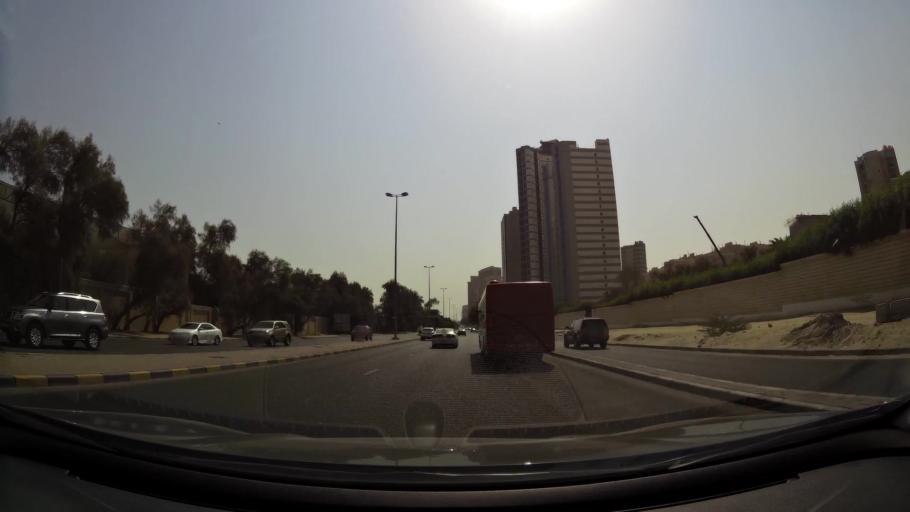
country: KW
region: Al Ahmadi
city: Al Fintas
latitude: 29.1585
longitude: 48.1226
